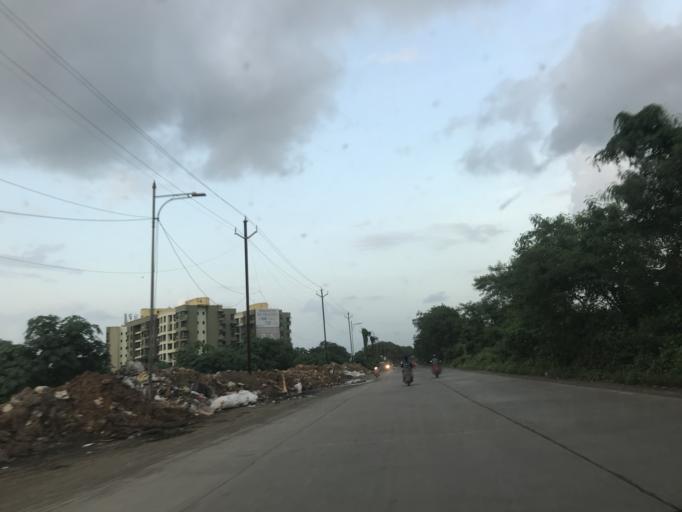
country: IN
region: Maharashtra
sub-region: Thane
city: Thane
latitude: 19.2248
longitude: 72.9951
